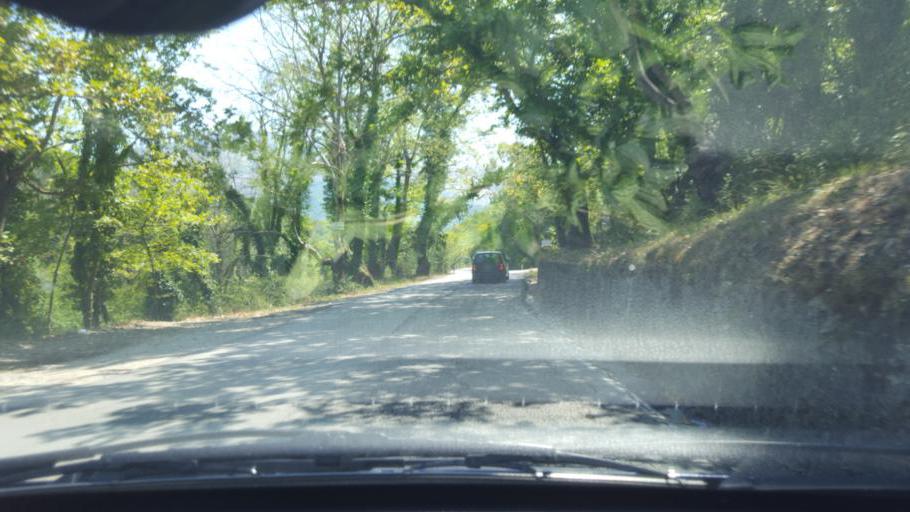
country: AL
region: Vlore
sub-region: Rrethi i Delvines
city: Mesopotam
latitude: 39.9200
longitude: 20.1689
